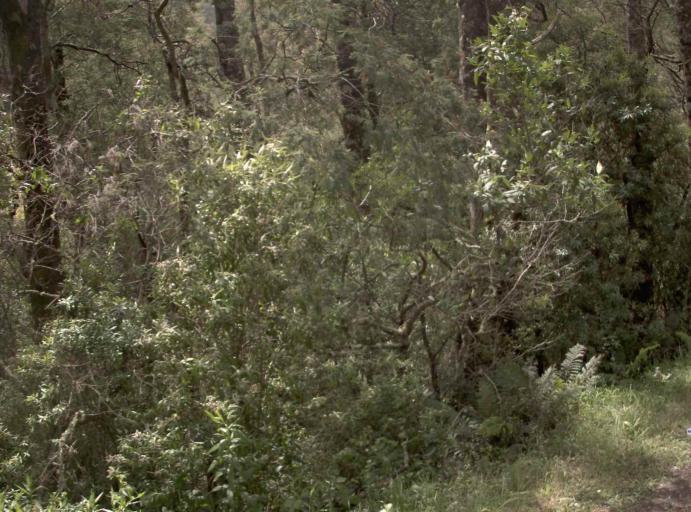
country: AU
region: Victoria
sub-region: Latrobe
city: Traralgon
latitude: -38.4267
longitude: 146.5659
